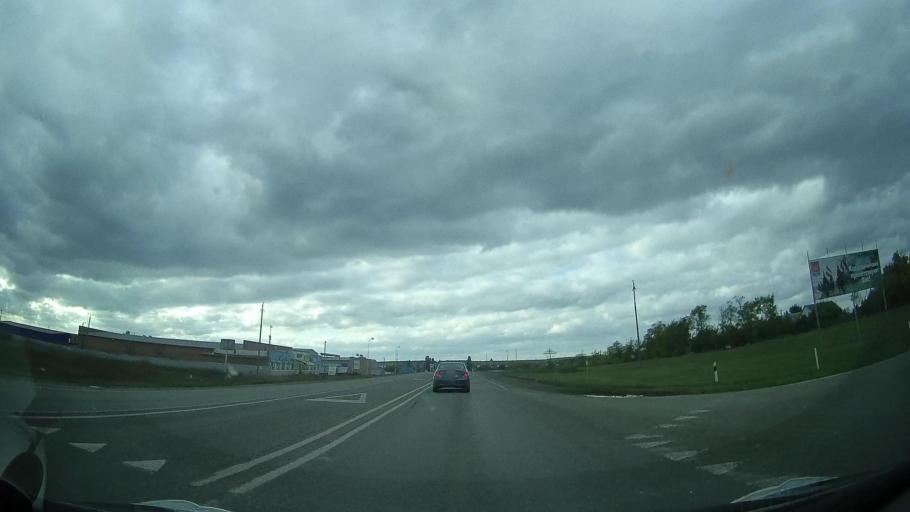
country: RU
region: Rostov
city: Kagal'nitskaya
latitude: 46.8746
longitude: 40.1613
